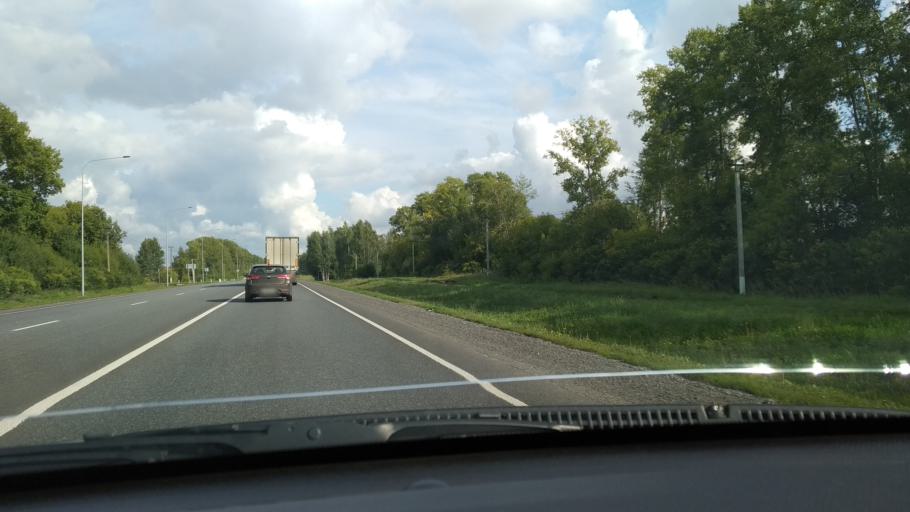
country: RU
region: Tatarstan
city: Stolbishchi
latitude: 55.6533
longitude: 49.3182
